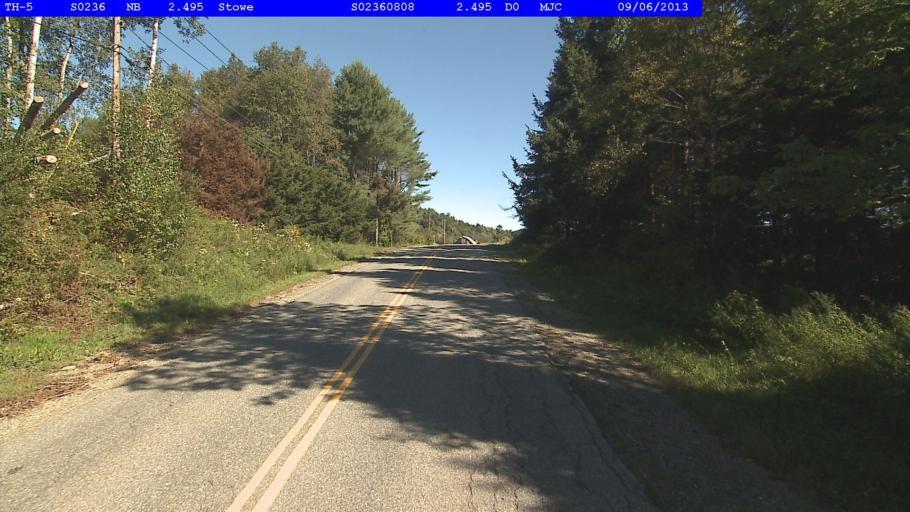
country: US
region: Vermont
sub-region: Washington County
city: Waterbury
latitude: 44.4608
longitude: -72.7290
